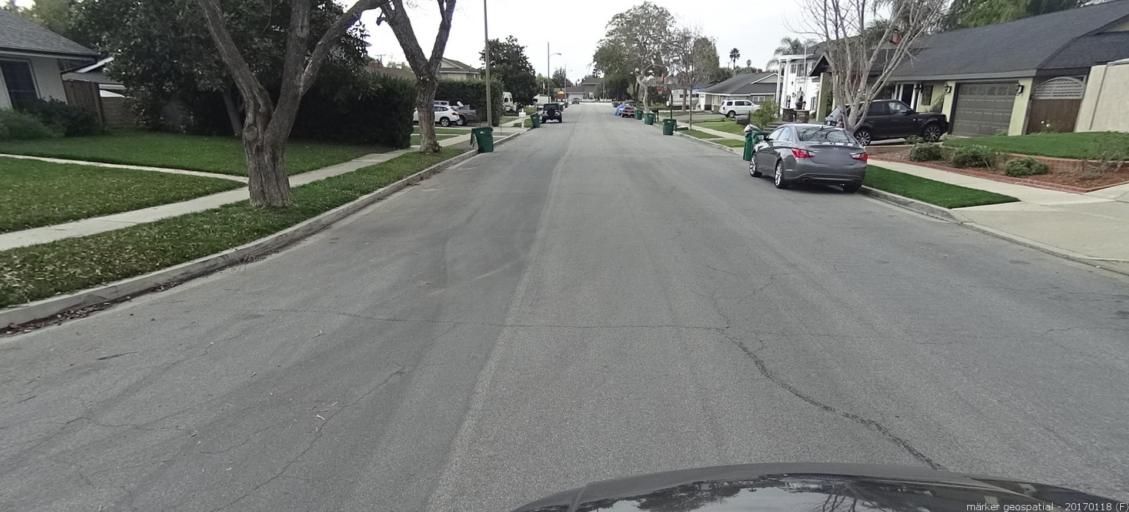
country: US
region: California
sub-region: Orange County
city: North Tustin
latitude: 33.7611
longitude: -117.7962
